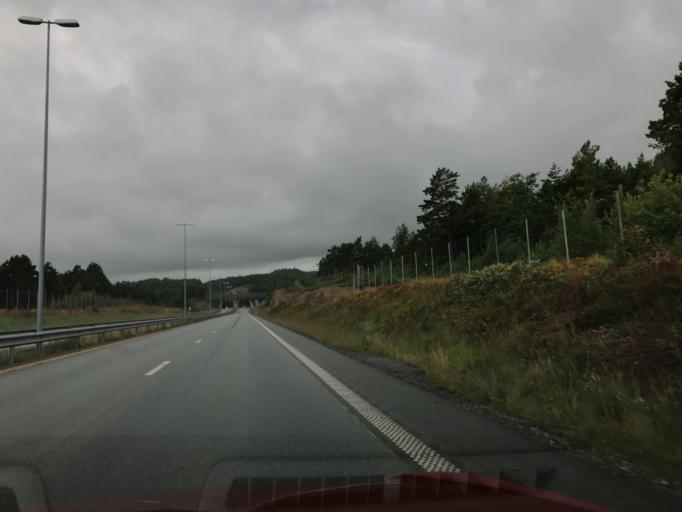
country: NO
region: Aust-Agder
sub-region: Lillesand
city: Lillesand
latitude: 58.2840
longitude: 8.4213
